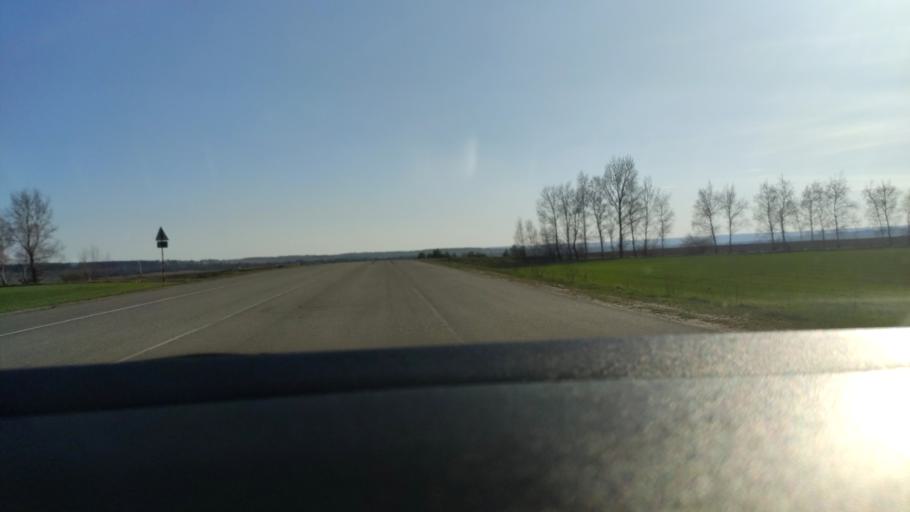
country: RU
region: Voronezj
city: Kolodeznyy
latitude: 51.3947
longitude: 39.2326
